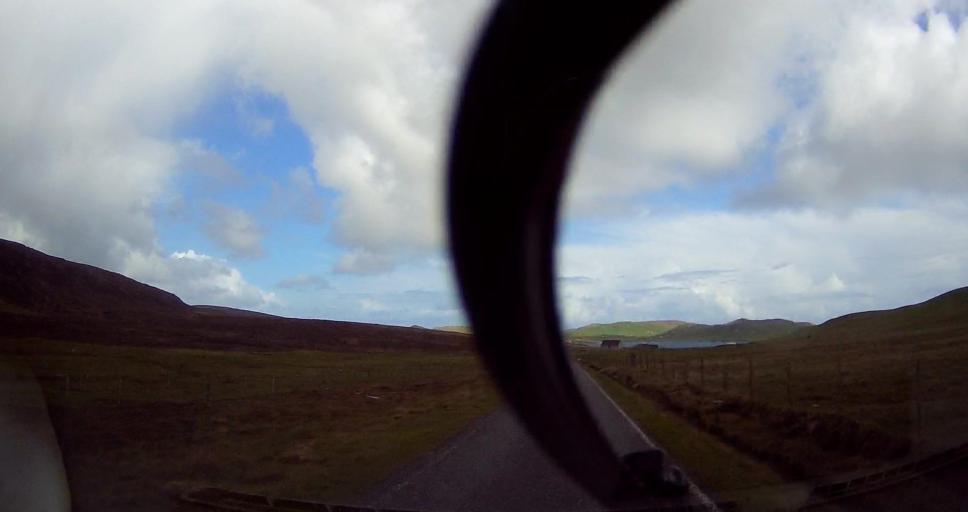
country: GB
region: Scotland
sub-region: Shetland Islands
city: Lerwick
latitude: 60.5682
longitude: -1.3337
